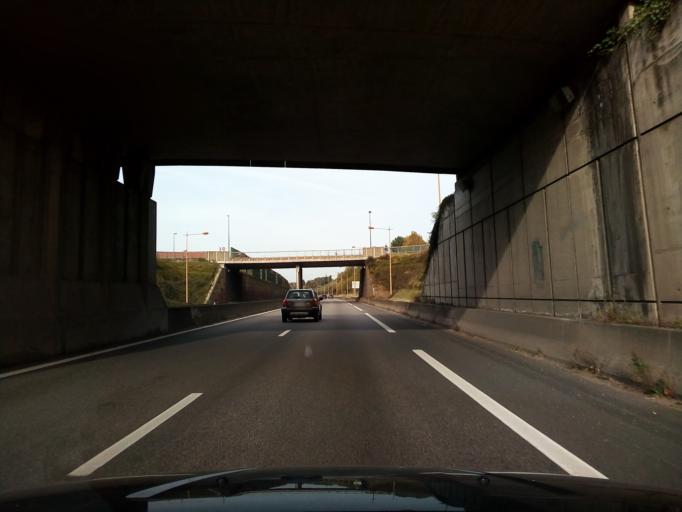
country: FR
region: Rhone-Alpes
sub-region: Departement de la Loire
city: Roanne
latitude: 46.0575
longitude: 4.0732
